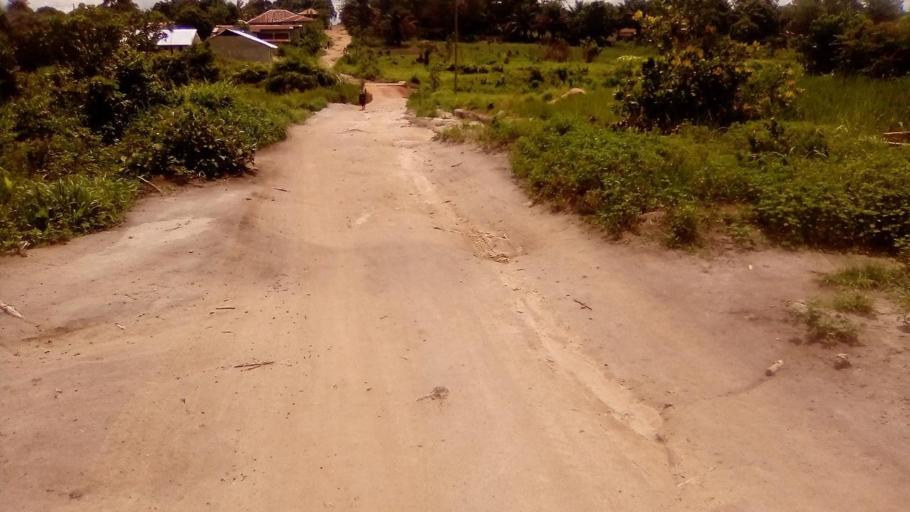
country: SL
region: Southern Province
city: Bo
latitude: 7.9362
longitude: -11.7449
